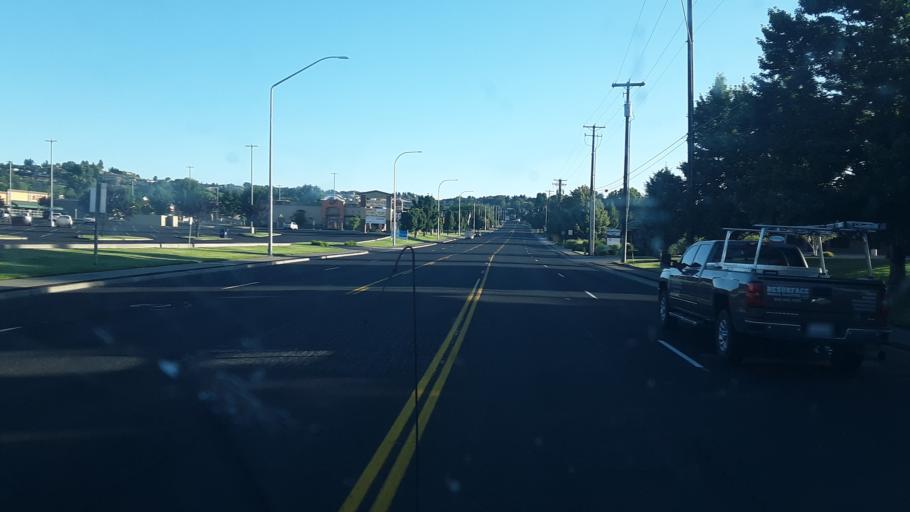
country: US
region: Washington
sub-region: Yakima County
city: West Valley
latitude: 46.5931
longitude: -120.6043
